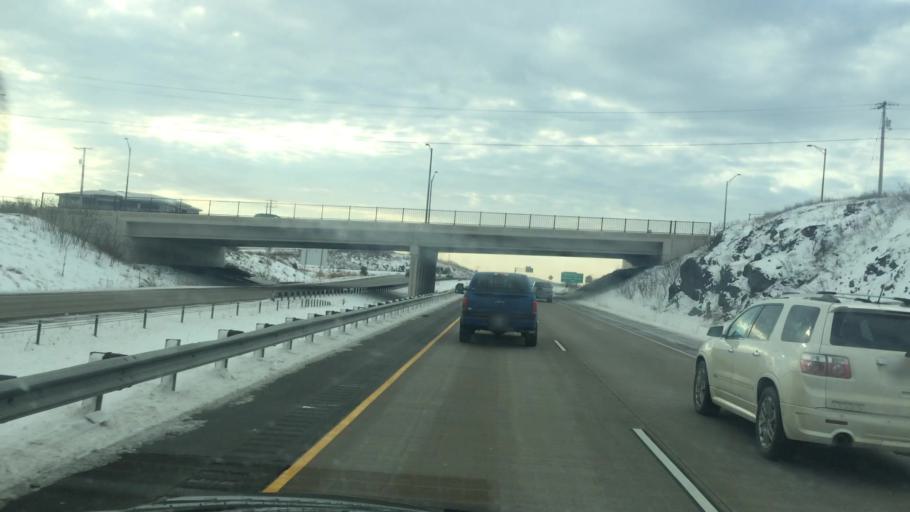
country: US
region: Wisconsin
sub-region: Marathon County
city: Wausau
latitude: 44.9707
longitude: -89.6567
